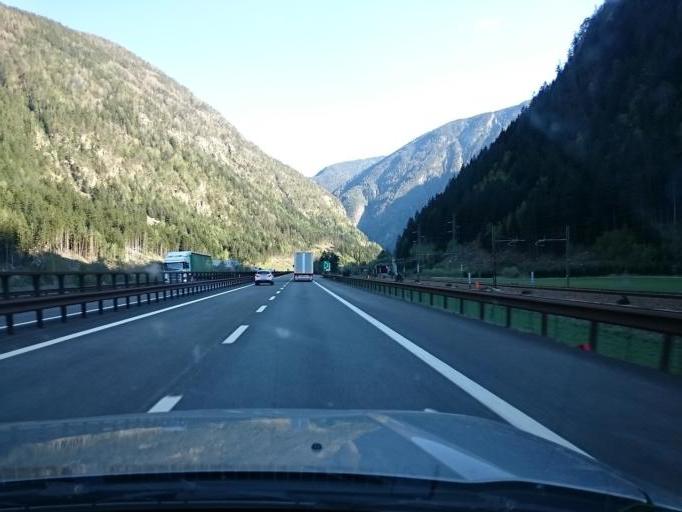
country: IT
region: Trentino-Alto Adige
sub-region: Bolzano
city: Campo di Trens
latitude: 46.8331
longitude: 11.5322
